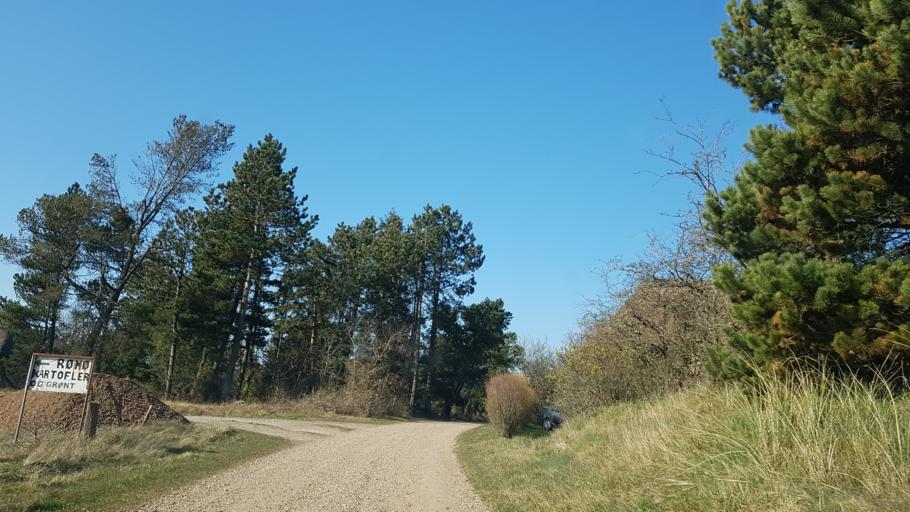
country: DE
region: Schleswig-Holstein
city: List
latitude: 55.0992
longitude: 8.5349
